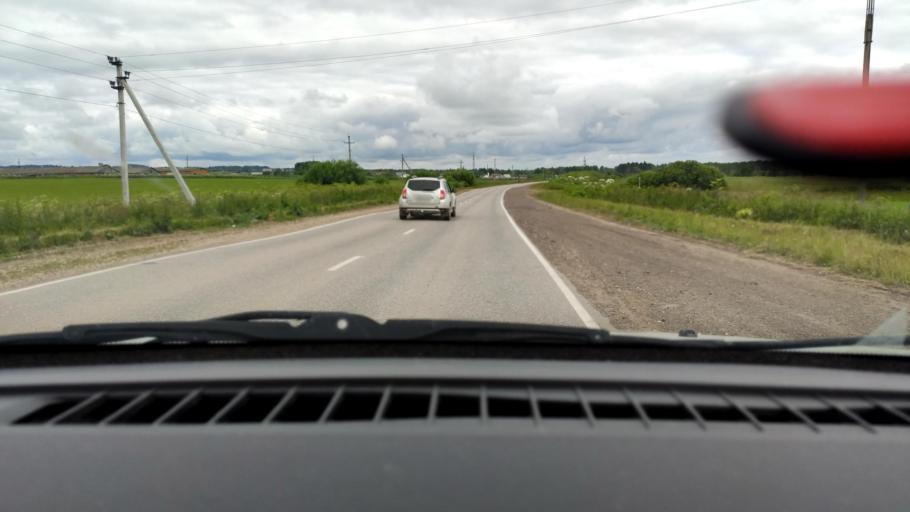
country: RU
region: Perm
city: Ust'-Kachka
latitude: 58.0750
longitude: 55.6210
